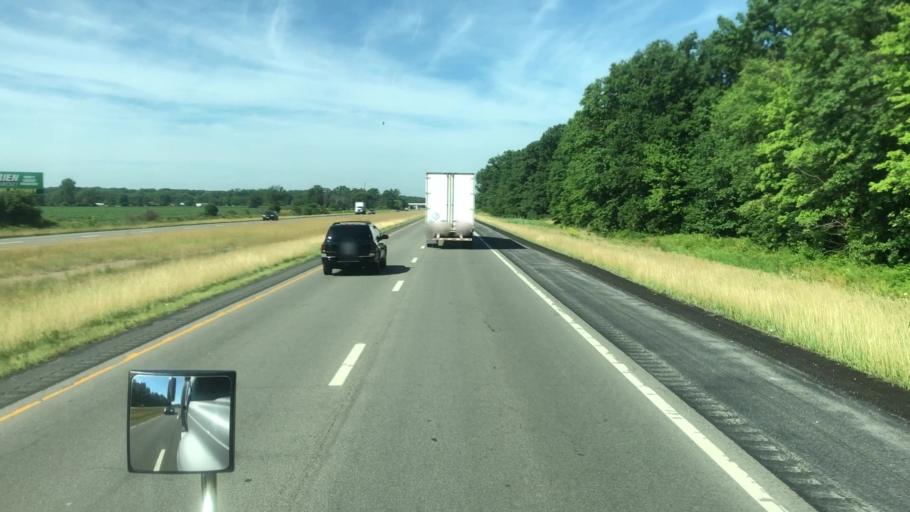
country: US
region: Ohio
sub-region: Lorain County
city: Vermilion
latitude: 41.3945
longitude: -82.3967
